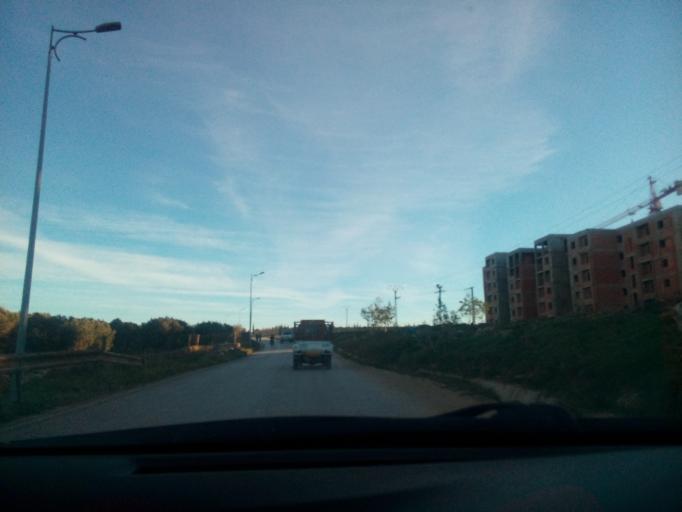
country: DZ
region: Oran
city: Es Senia
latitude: 35.6279
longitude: -0.6762
